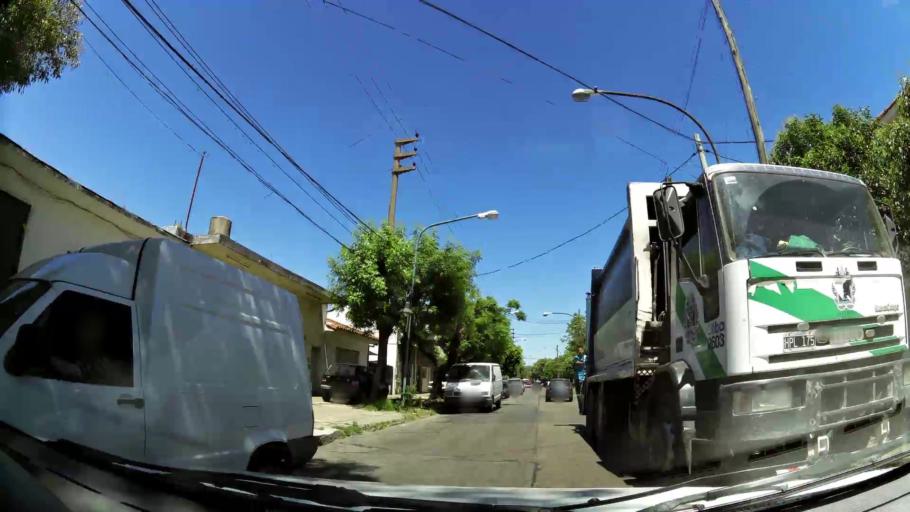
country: AR
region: Buenos Aires
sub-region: Partido de Vicente Lopez
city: Olivos
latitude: -34.5146
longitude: -58.5315
